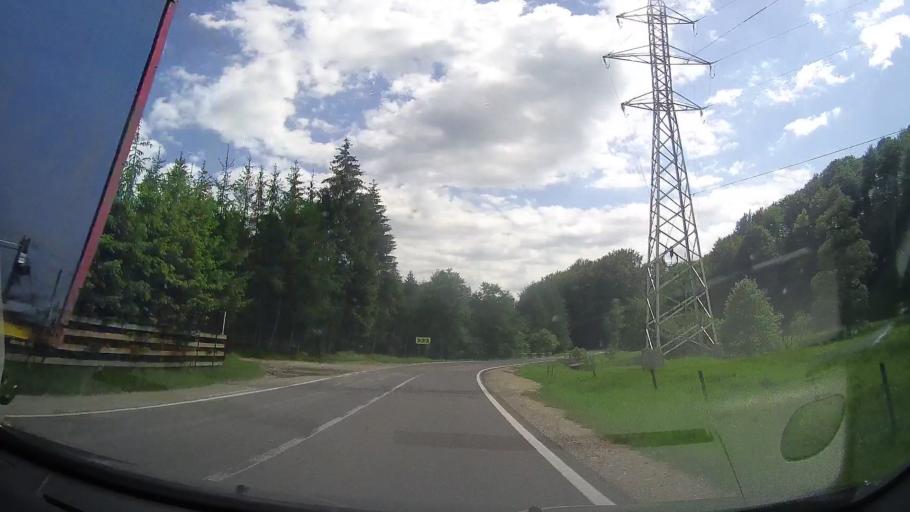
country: RO
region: Prahova
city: Maneciu
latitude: 45.4151
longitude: 25.9428
